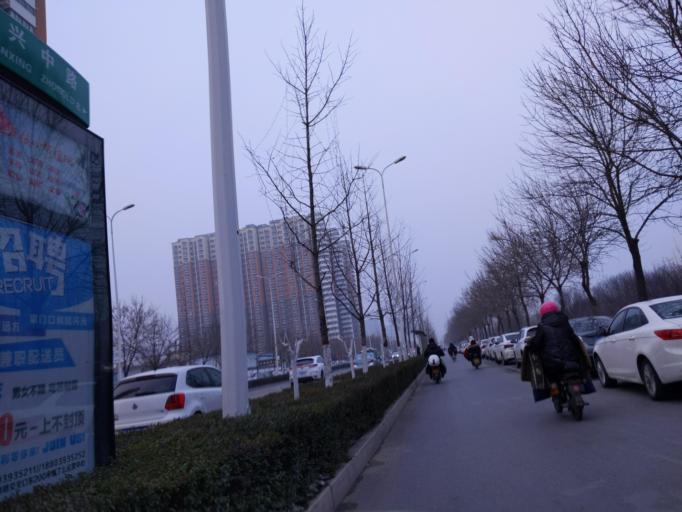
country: CN
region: Henan Sheng
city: Puyang
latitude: 35.7770
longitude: 115.0264
